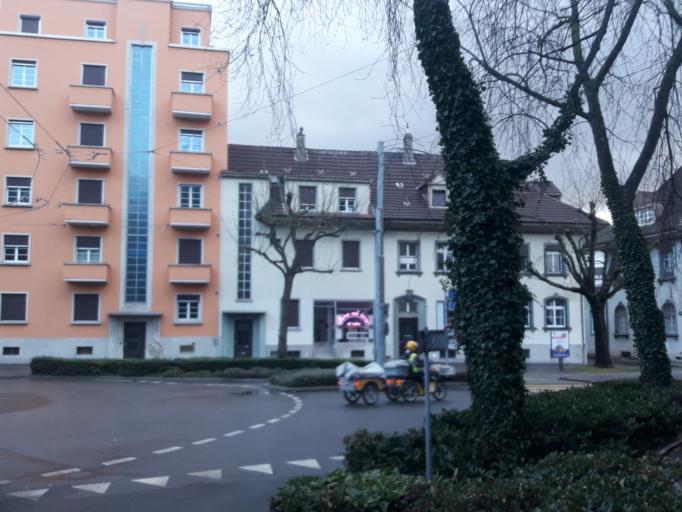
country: CH
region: Bern
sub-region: Biel/Bienne District
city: Biel/Bienne
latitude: 47.1325
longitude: 7.2461
